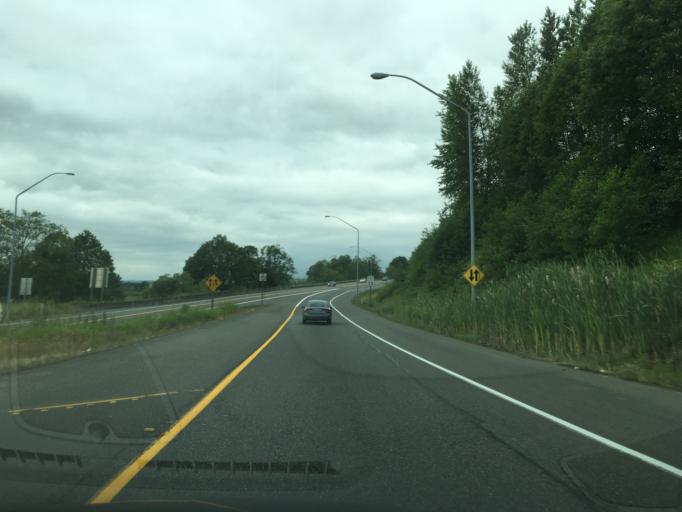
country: US
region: Washington
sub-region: Snohomish County
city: Fobes Hill
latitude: 47.9797
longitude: -122.1373
